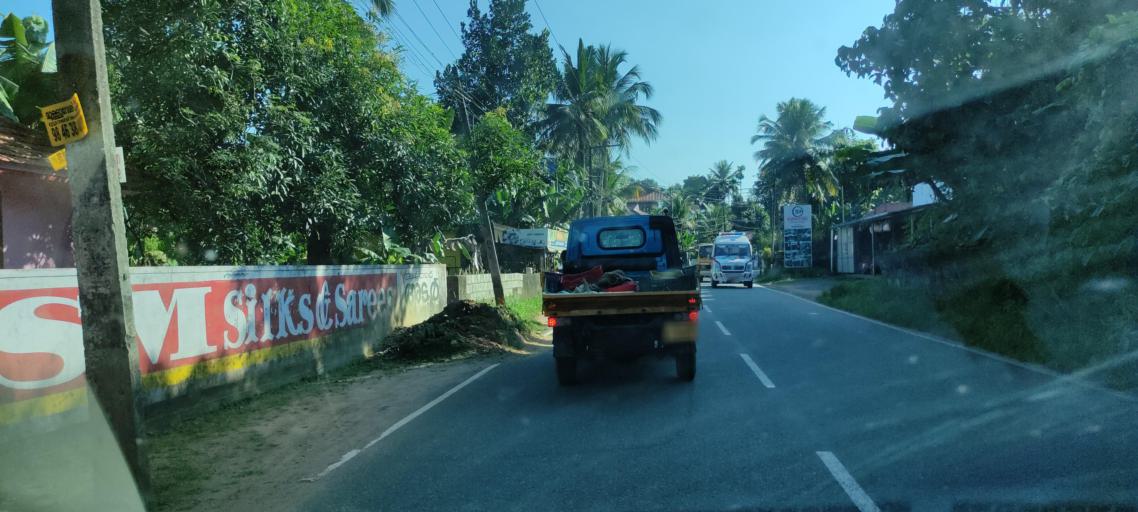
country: IN
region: Kerala
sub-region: Pattanamtitta
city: Adur
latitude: 9.2059
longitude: 76.7468
